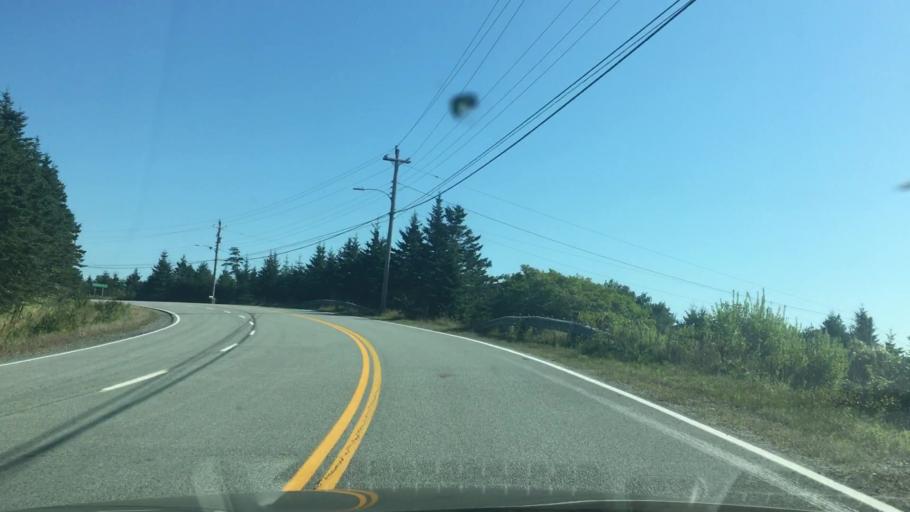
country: CA
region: Nova Scotia
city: New Glasgow
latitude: 44.8140
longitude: -62.6326
